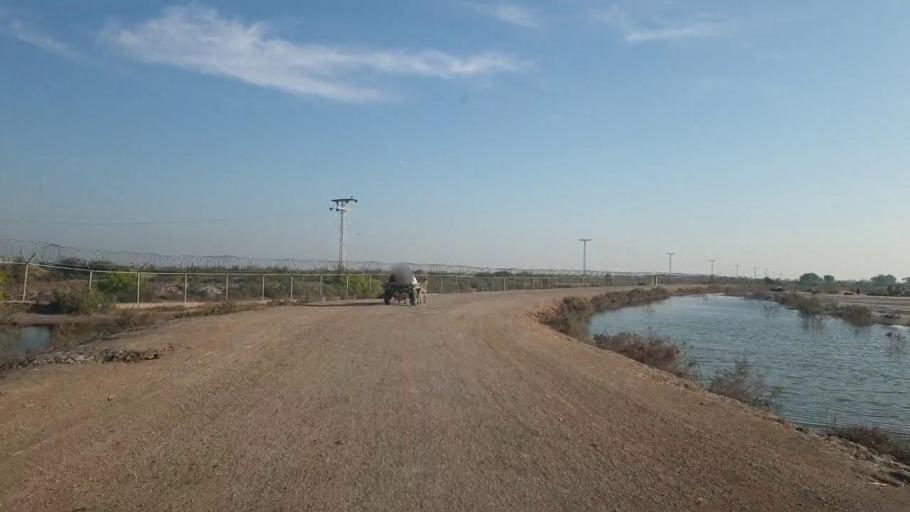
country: PK
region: Sindh
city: Talhar
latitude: 24.8391
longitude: 68.8474
